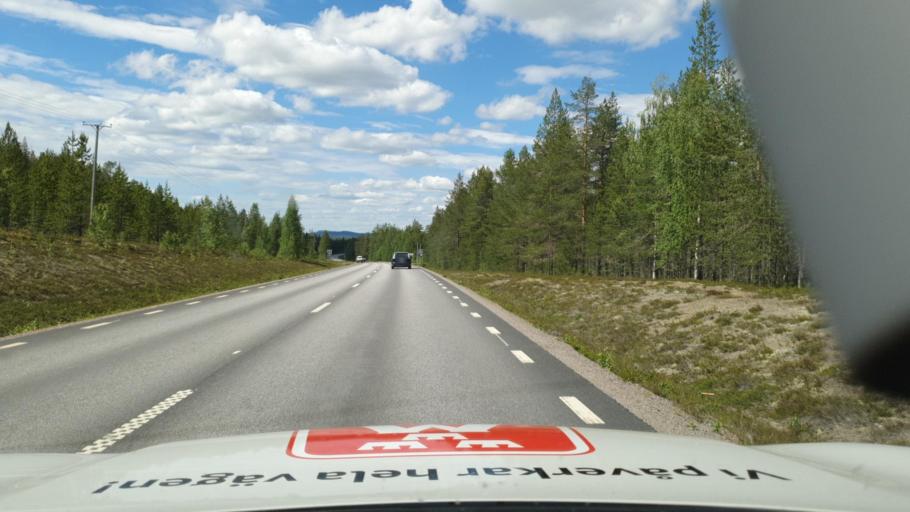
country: SE
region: Vaesterbotten
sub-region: Skelleftea Kommun
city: Langsele
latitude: 65.0190
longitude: 20.1423
